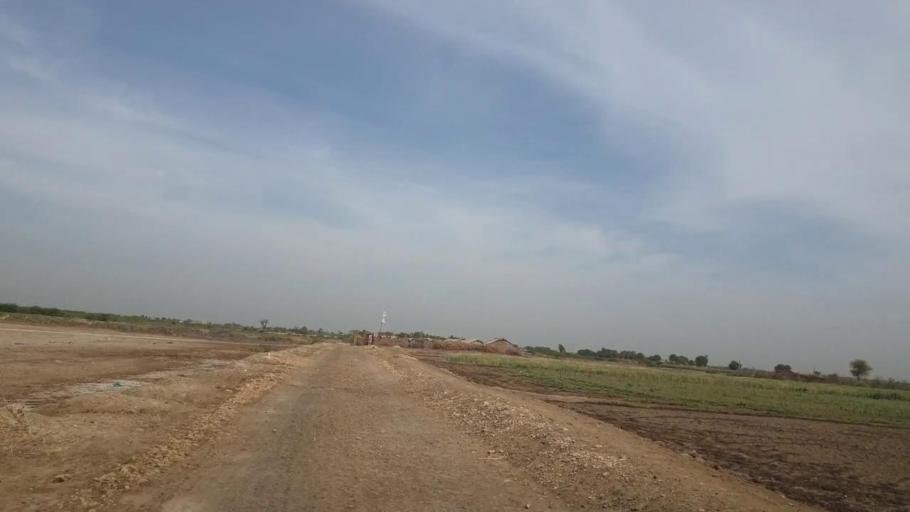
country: PK
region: Sindh
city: Kunri
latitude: 25.1791
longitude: 69.5856
